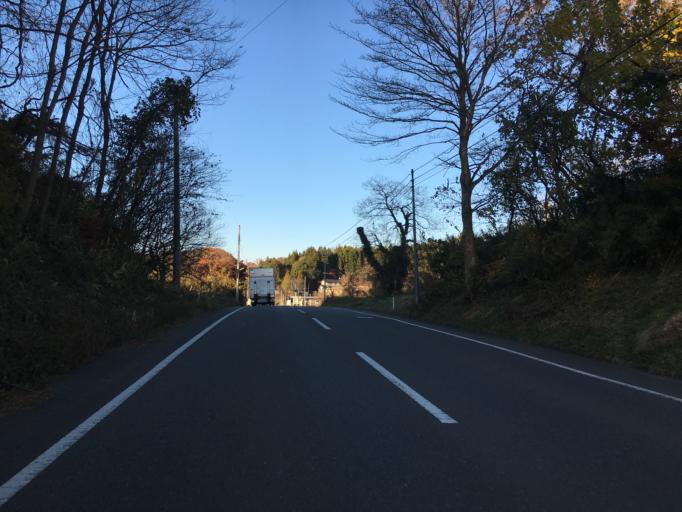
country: JP
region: Fukushima
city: Sukagawa
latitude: 37.3267
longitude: 140.4404
